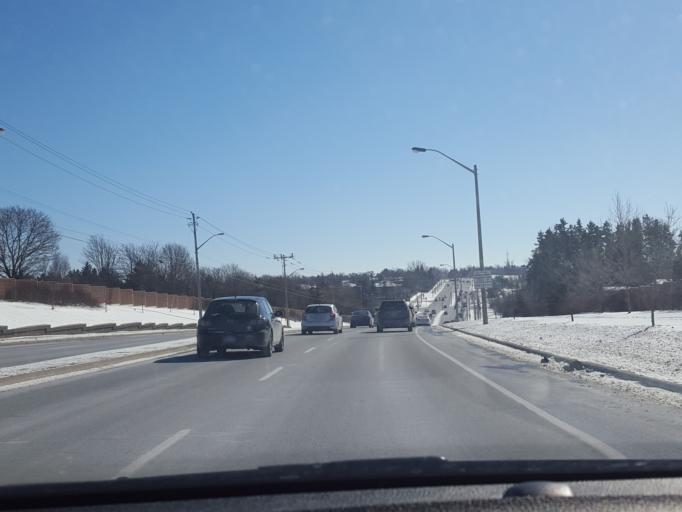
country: CA
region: Ontario
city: Kitchener
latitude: 43.4356
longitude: -80.5281
